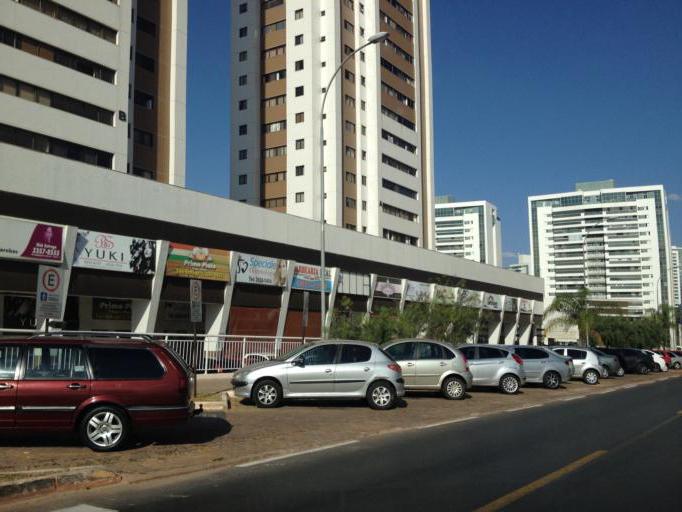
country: BR
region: Federal District
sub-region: Brasilia
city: Brasilia
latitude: -15.8318
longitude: -48.0358
